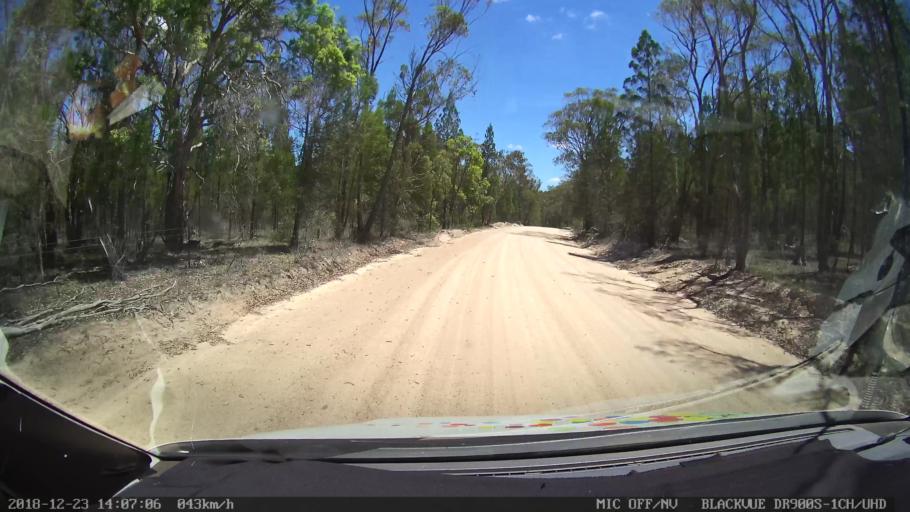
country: AU
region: New South Wales
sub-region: Tamworth Municipality
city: Manilla
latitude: -30.6339
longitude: 151.0732
